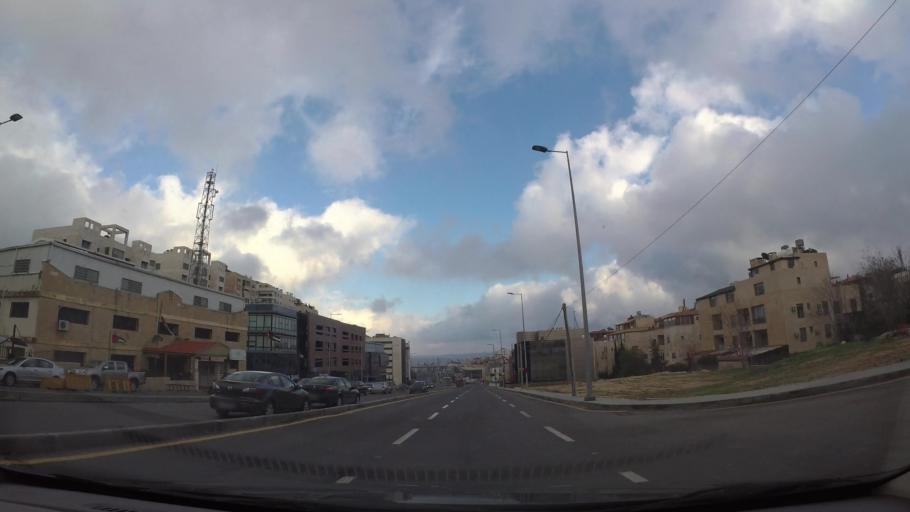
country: JO
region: Amman
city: Wadi as Sir
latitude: 31.9564
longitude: 35.8820
